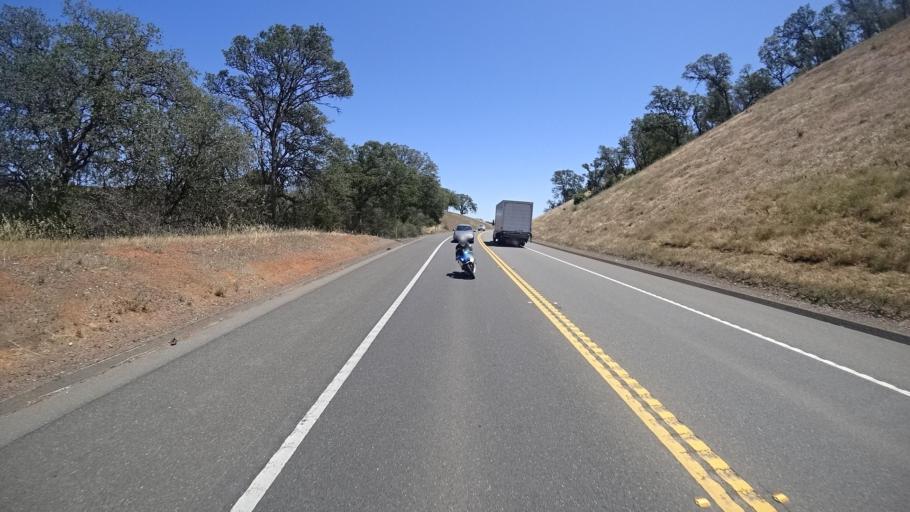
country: US
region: California
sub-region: Lake County
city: Clearlake
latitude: 39.0062
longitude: -122.6089
